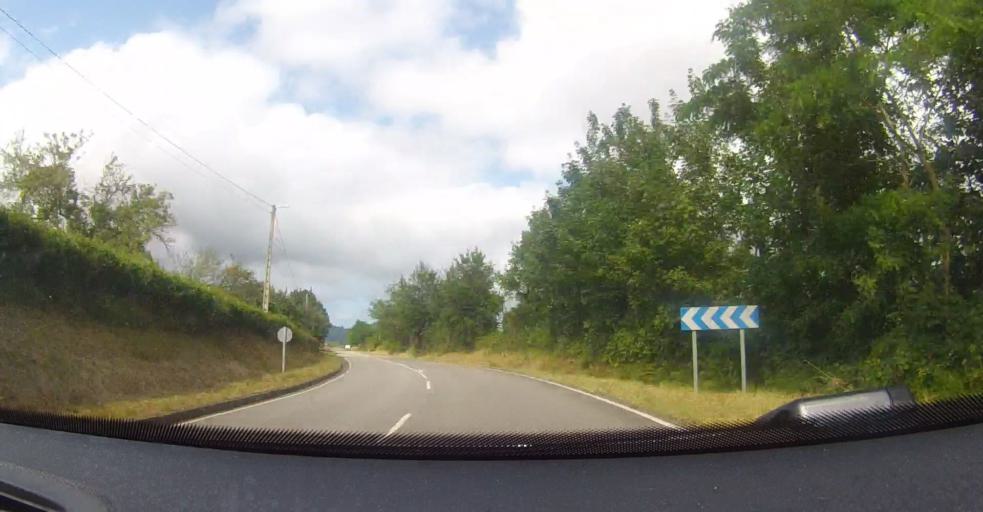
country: ES
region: Asturias
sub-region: Province of Asturias
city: Villaviciosa
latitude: 43.4946
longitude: -5.4294
